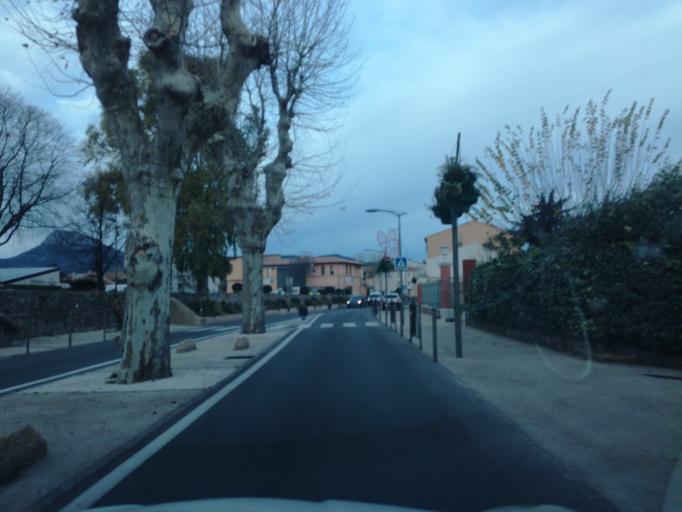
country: FR
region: Provence-Alpes-Cote d'Azur
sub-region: Departement du Var
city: La Crau
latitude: 43.1474
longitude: 6.0763
